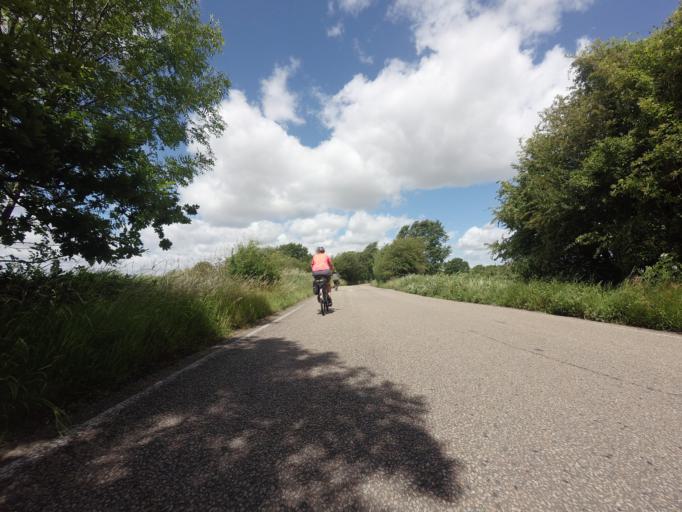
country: GB
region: England
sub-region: Kent
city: Strood
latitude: 51.4315
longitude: 0.4608
